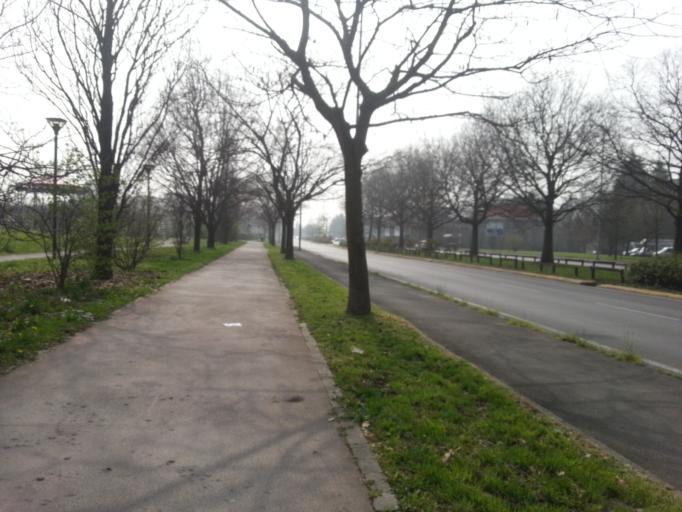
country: IT
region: Lombardy
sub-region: Citta metropolitana di Milano
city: Cusano Milanino
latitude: 45.5579
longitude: 9.1994
